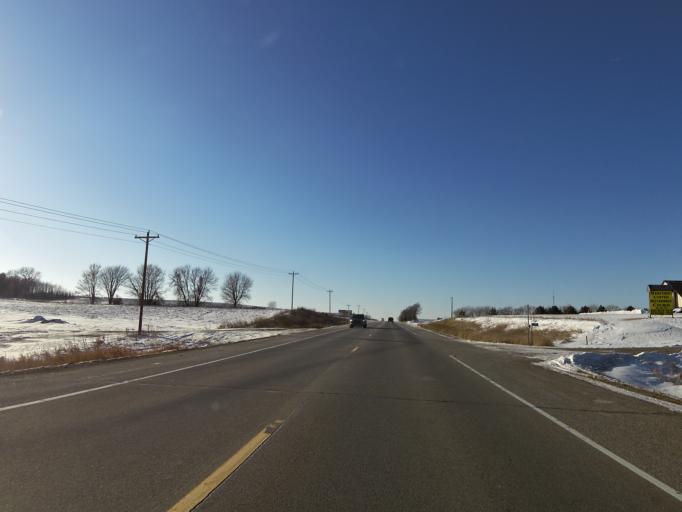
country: US
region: Minnesota
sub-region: Le Sueur County
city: New Prague
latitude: 44.5436
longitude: -93.5174
